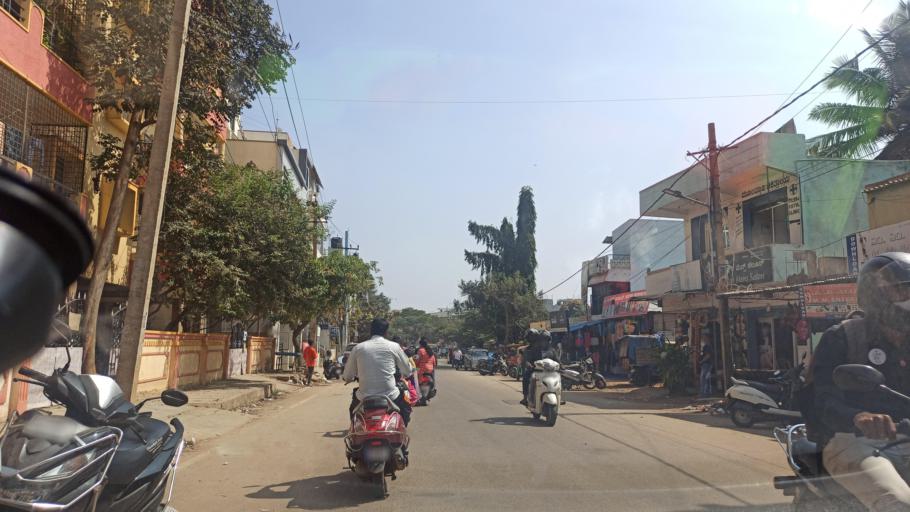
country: IN
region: Karnataka
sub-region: Bangalore Urban
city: Yelahanka
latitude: 13.0663
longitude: 77.5972
